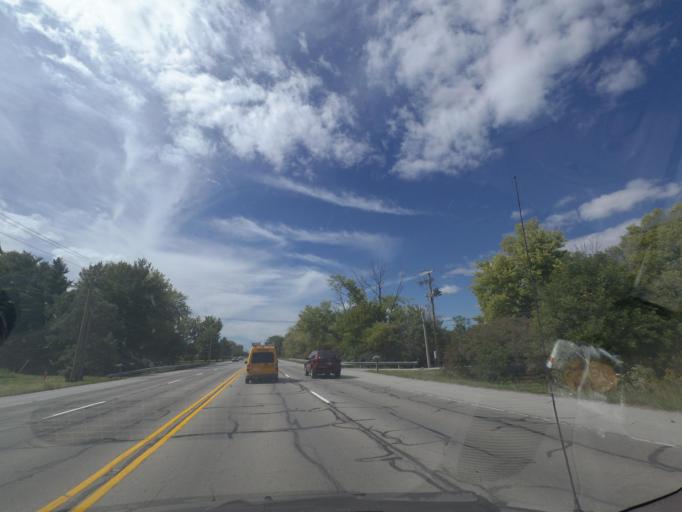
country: US
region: Indiana
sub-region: Marion County
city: Cumberland
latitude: 39.7781
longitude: -85.9233
